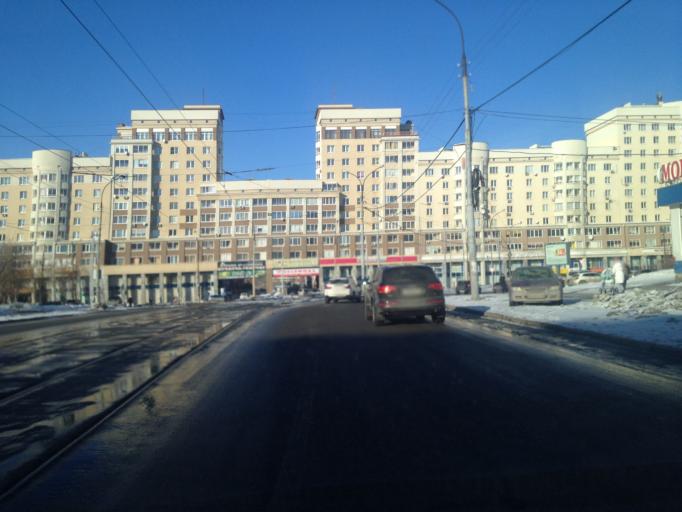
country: RU
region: Sverdlovsk
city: Yekaterinburg
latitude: 56.8352
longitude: 60.5457
